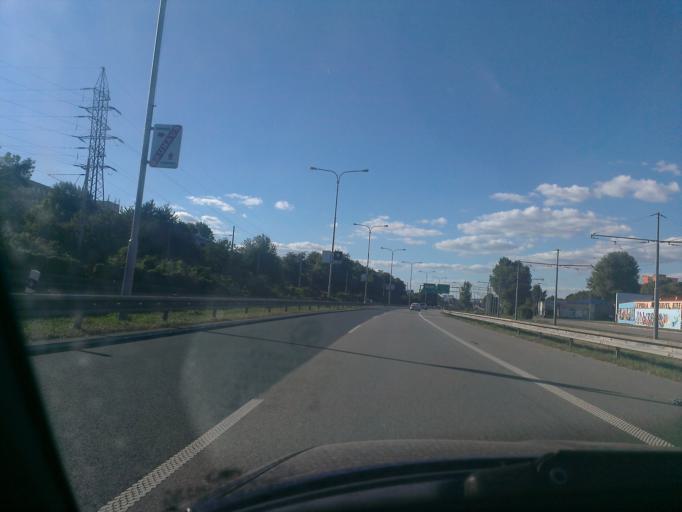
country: CZ
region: South Moravian
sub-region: Mesto Brno
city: Brno
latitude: 49.1878
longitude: 16.6565
